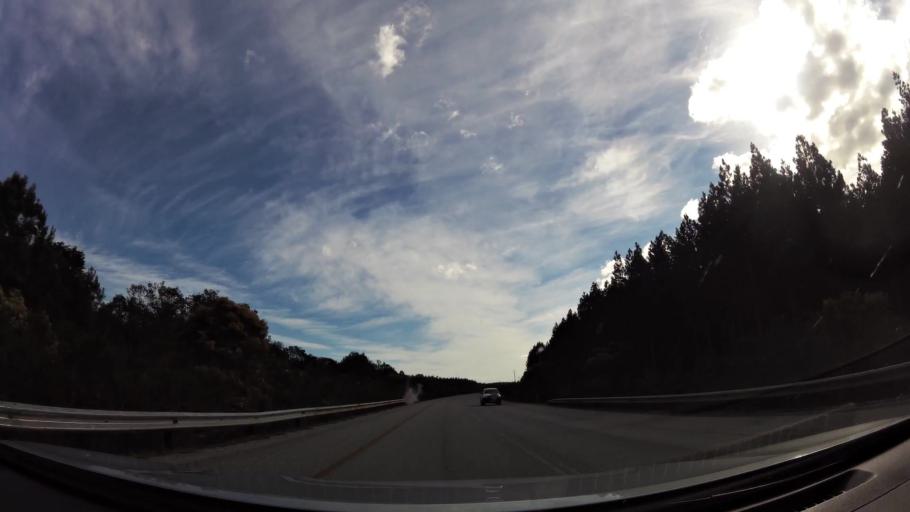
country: ZA
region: Eastern Cape
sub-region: Cacadu District Municipality
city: Kareedouw
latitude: -33.9908
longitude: 24.0907
